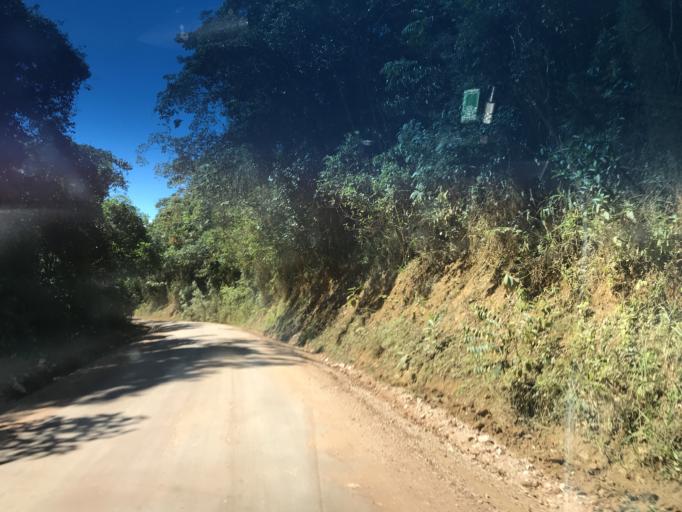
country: BR
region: Bahia
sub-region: Mutuipe
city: Mutuipe
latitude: -13.3741
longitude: -39.3777
